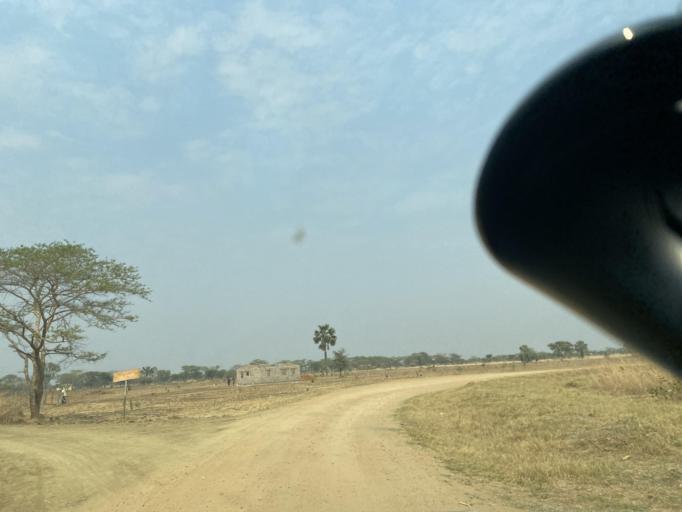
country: ZM
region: Lusaka
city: Kafue
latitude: -15.6529
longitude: 28.0540
